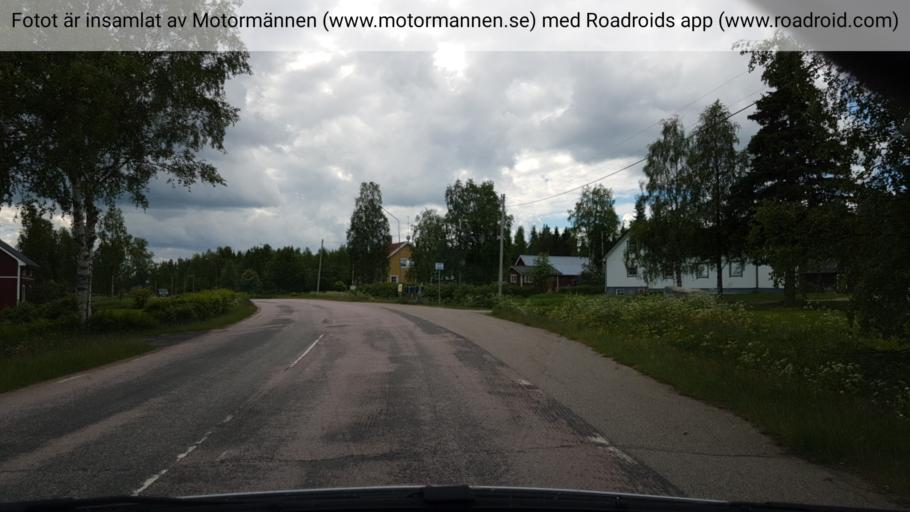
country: FI
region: Lapland
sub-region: Torniolaakso
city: Ylitornio
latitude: 66.1958
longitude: 23.7117
